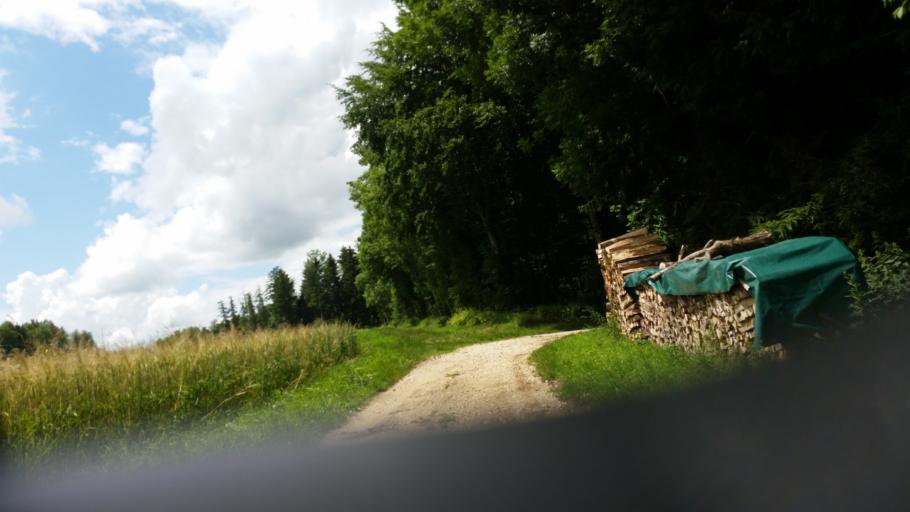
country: CH
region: Vaud
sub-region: Jura-Nord vaudois District
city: Yverdon-les-Bains
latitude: 46.7486
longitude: 6.6718
